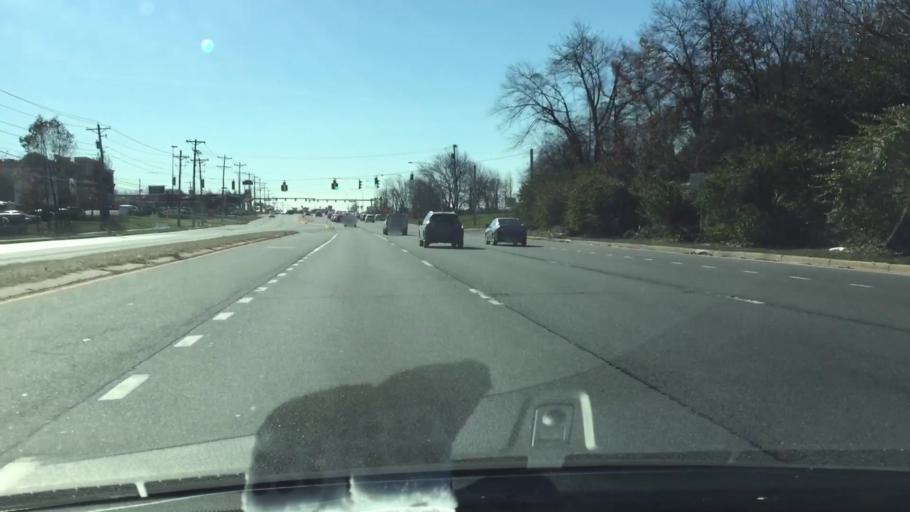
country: US
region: Delaware
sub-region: New Castle County
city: Bellefonte
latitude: 39.8322
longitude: -75.5435
